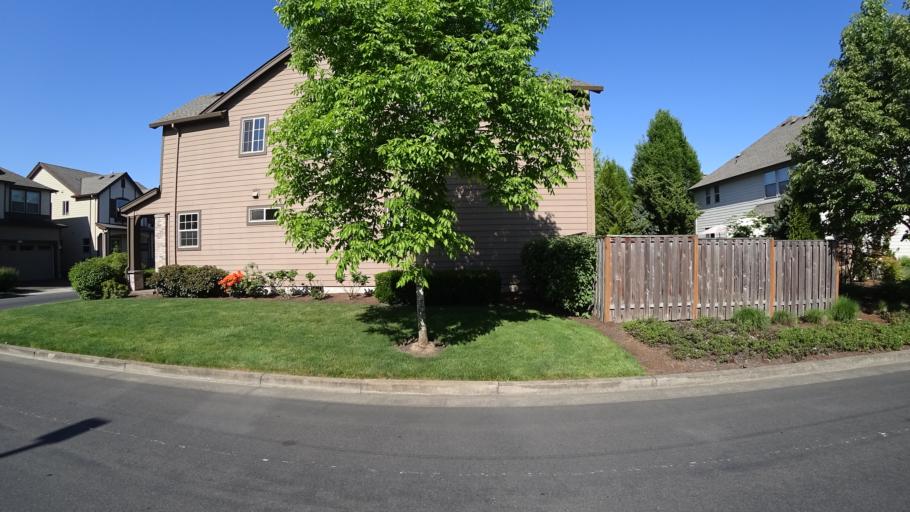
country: US
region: Oregon
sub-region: Washington County
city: Rockcreek
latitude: 45.5219
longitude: -122.9153
